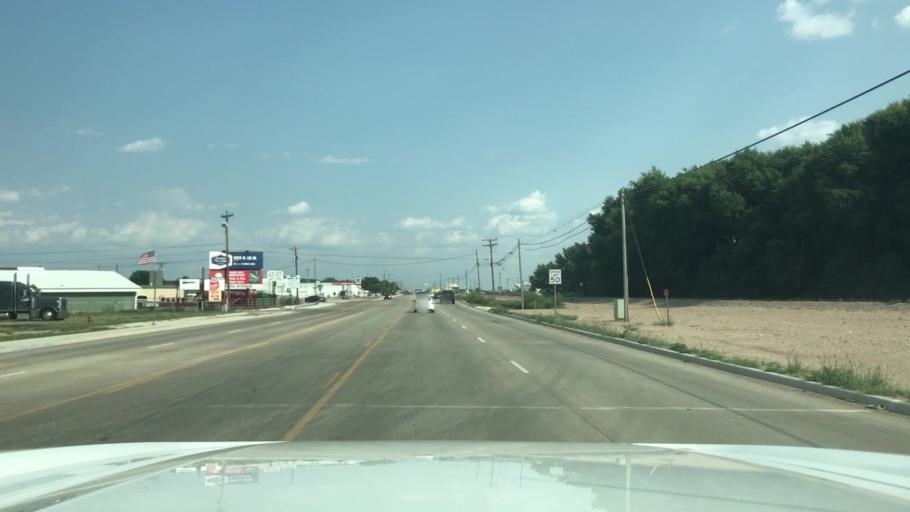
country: US
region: Texas
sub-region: Dallam County
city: Dalhart
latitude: 36.0550
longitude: -102.5067
